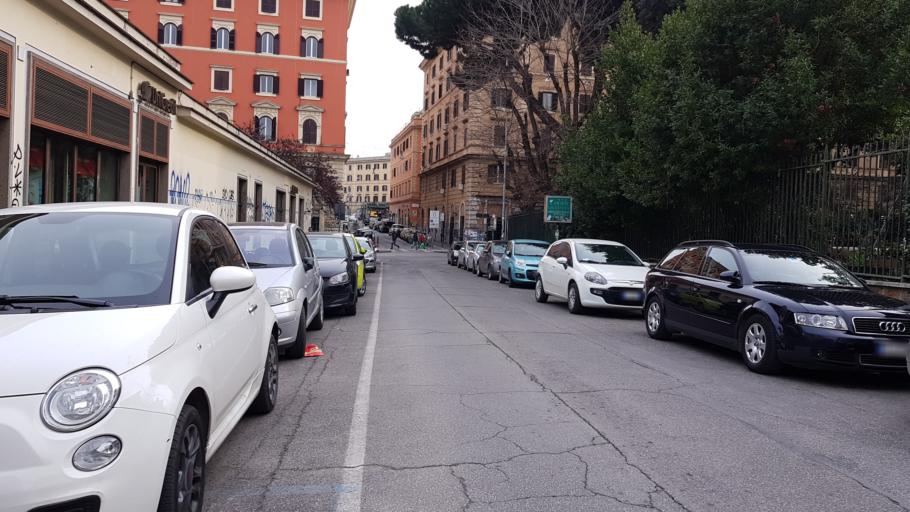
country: IT
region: Latium
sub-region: Citta metropolitana di Roma Capitale
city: Rome
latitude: 41.8985
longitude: 12.5132
